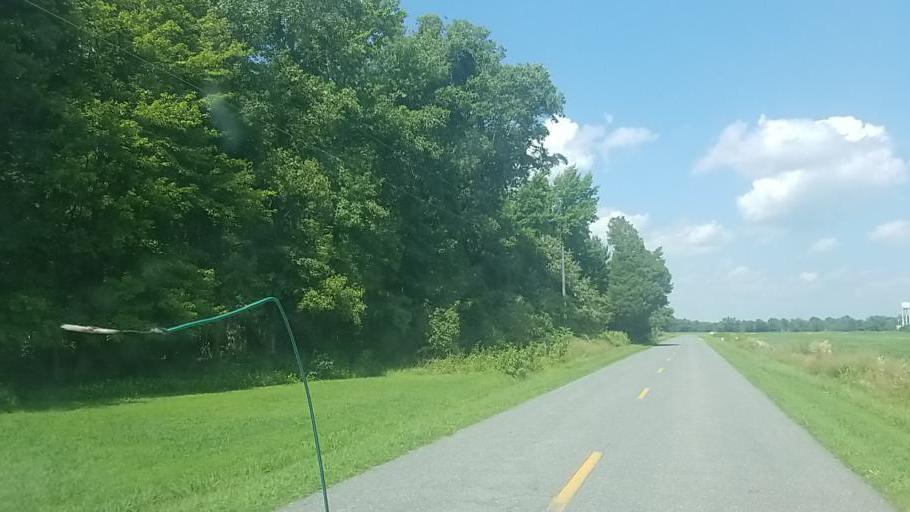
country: US
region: Maryland
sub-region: Dorchester County
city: Hurlock
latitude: 38.4761
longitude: -75.8390
